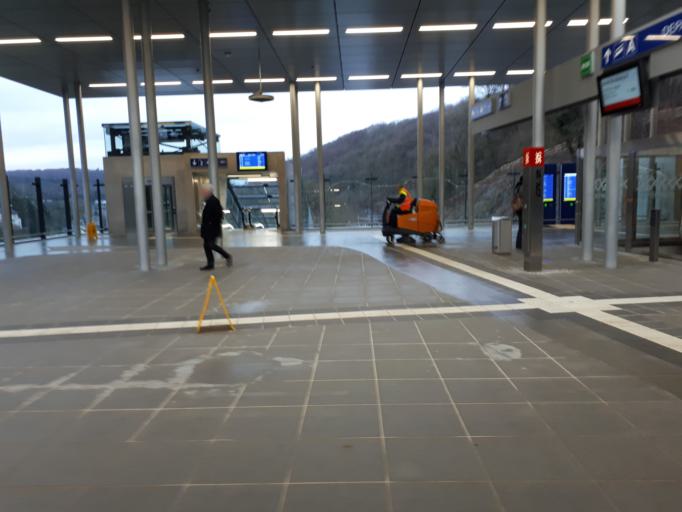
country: LU
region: Luxembourg
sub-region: Canton de Luxembourg
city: Luxembourg
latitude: 49.6187
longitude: 6.1329
